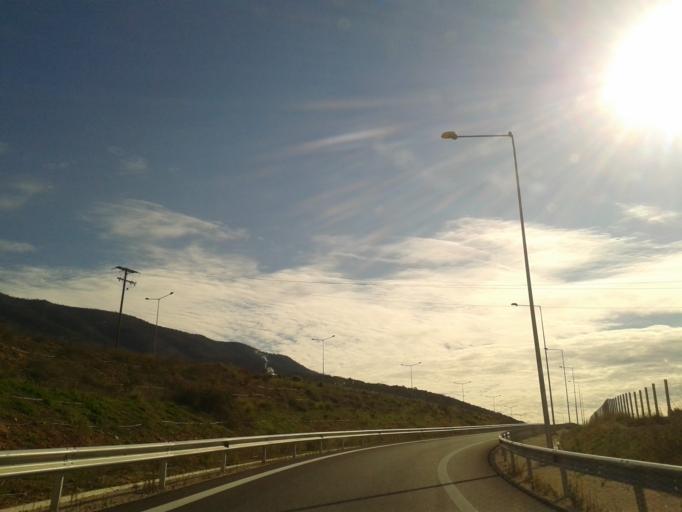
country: GR
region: West Greece
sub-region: Nomos Aitolias kai Akarnanias
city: Stanos
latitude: 38.7768
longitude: 21.1872
